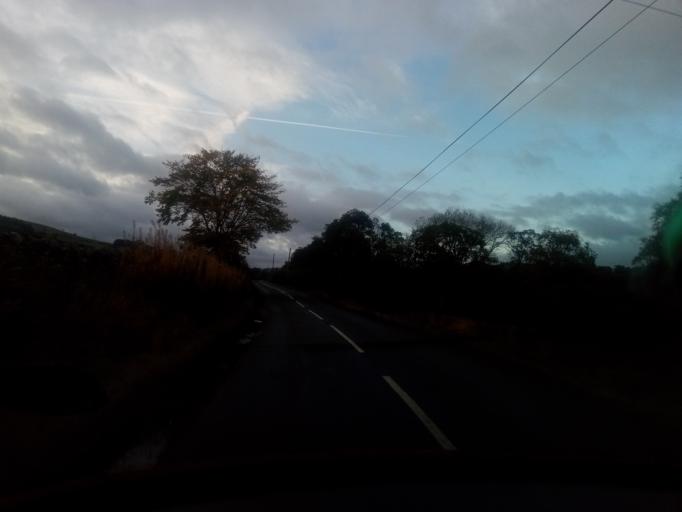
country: GB
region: Scotland
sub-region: The Scottish Borders
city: Jedburgh
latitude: 55.4166
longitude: -2.6359
